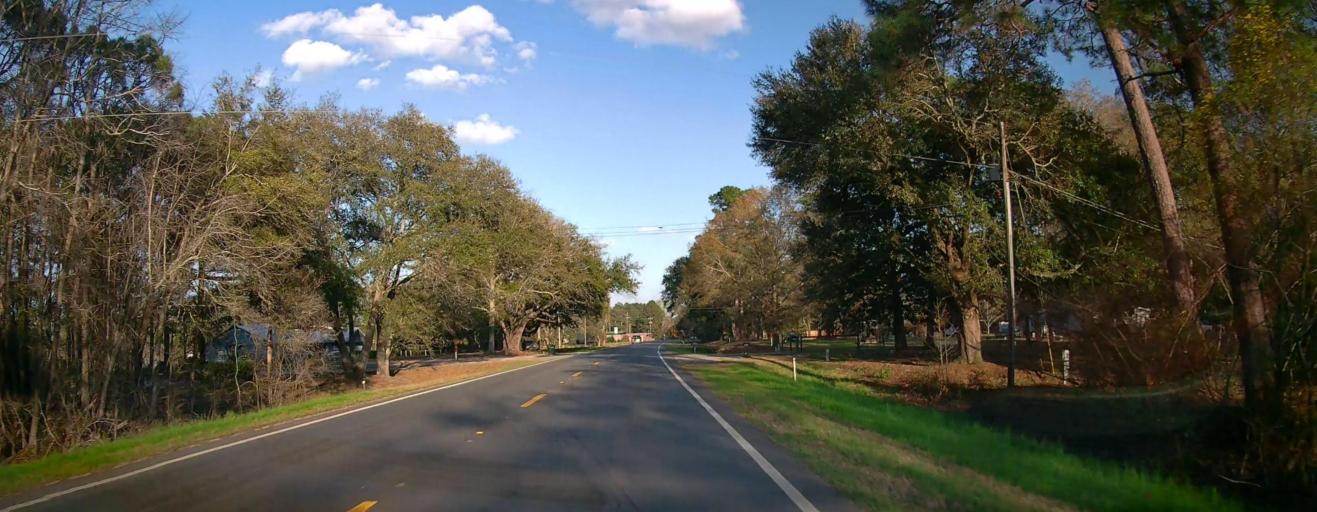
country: US
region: Georgia
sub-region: Evans County
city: Claxton
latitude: 32.1619
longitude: -81.8843
